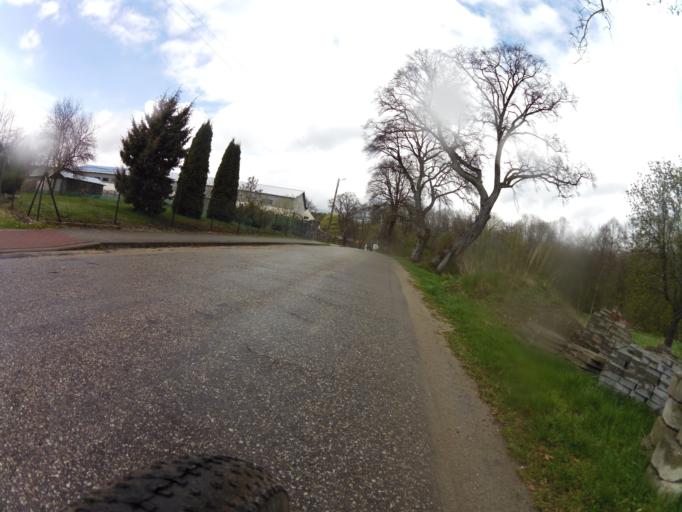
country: PL
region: Pomeranian Voivodeship
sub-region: Powiat slupski
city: Kepice
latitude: 54.2170
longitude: 16.7671
